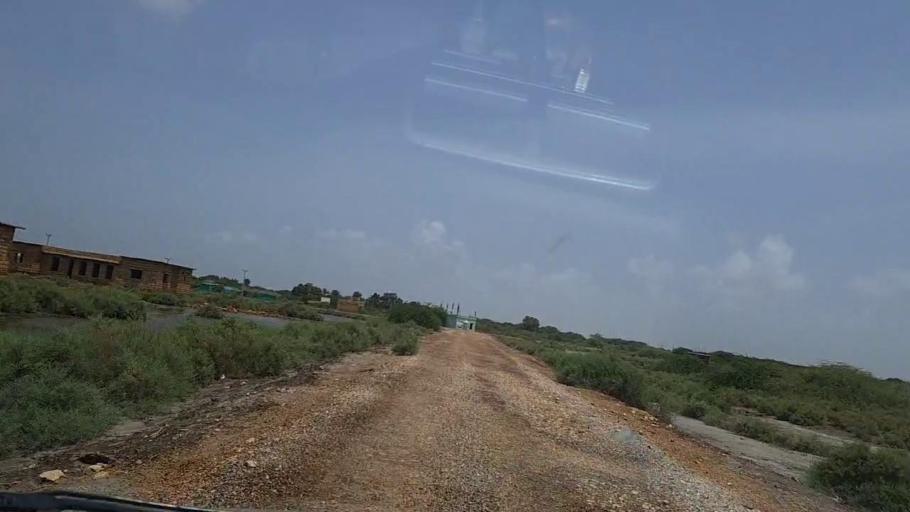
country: PK
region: Sindh
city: Keti Bandar
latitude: 24.1515
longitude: 67.5328
